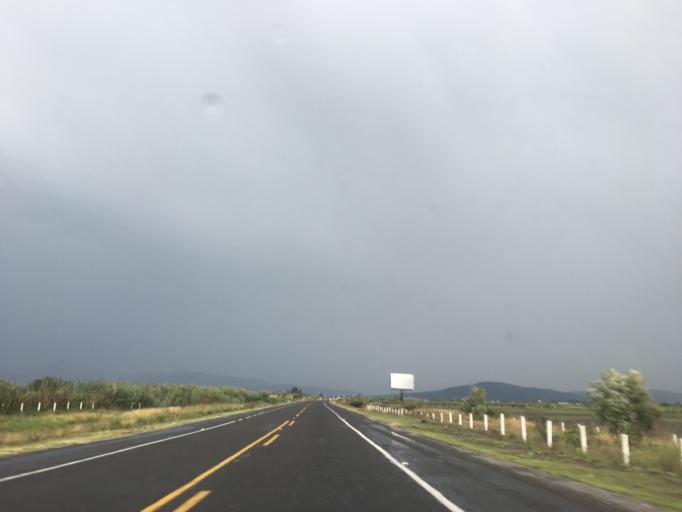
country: MX
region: Michoacan
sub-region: Alvaro Obregon
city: Lazaro Cardenas (La Purisima)
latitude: 19.8679
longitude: -101.0077
